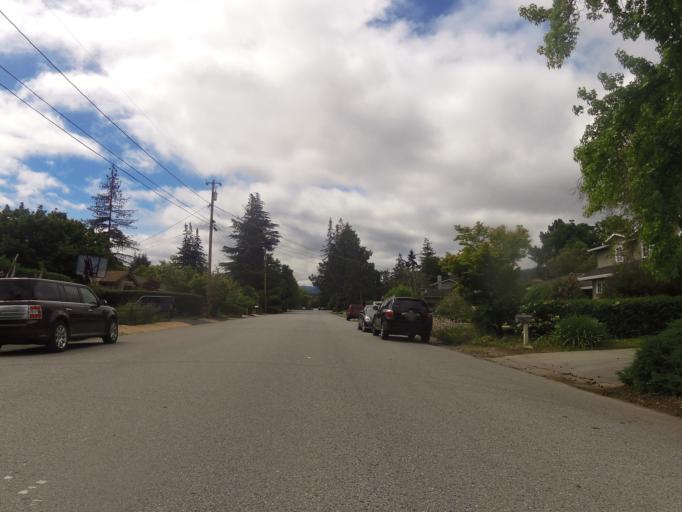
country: US
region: California
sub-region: Santa Clara County
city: Loyola
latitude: 37.3666
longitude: -122.0909
